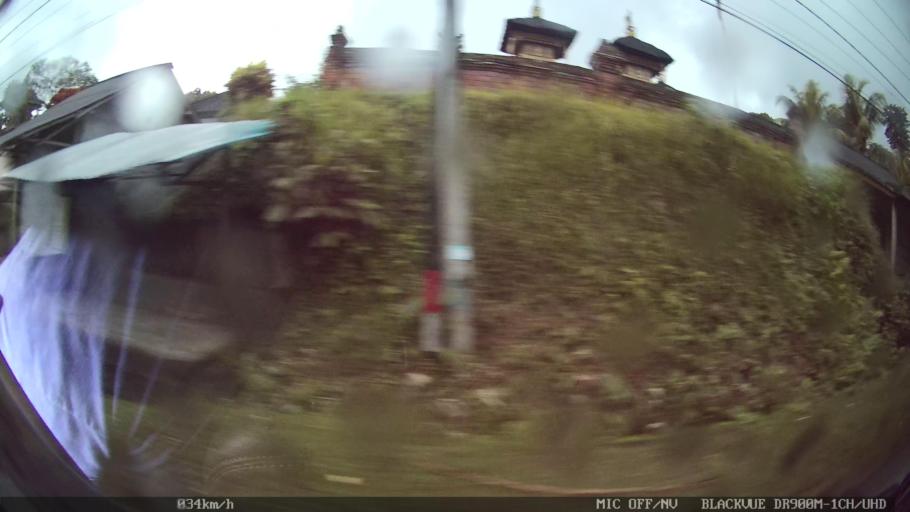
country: ID
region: Bali
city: Banjar Tengah
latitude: -8.4958
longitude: 115.1881
